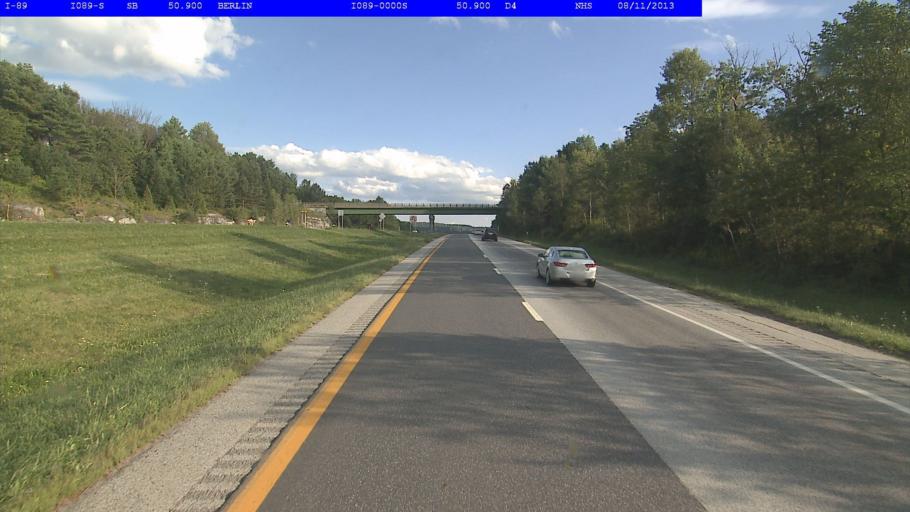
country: US
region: Vermont
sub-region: Washington County
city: Montpelier
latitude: 44.2244
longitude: -72.5859
